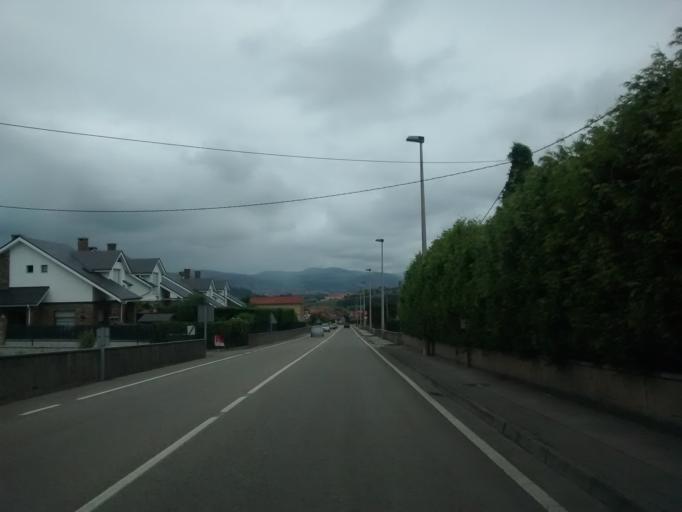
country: ES
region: Cantabria
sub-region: Provincia de Cantabria
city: Suances
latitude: 43.4030
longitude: -4.0480
